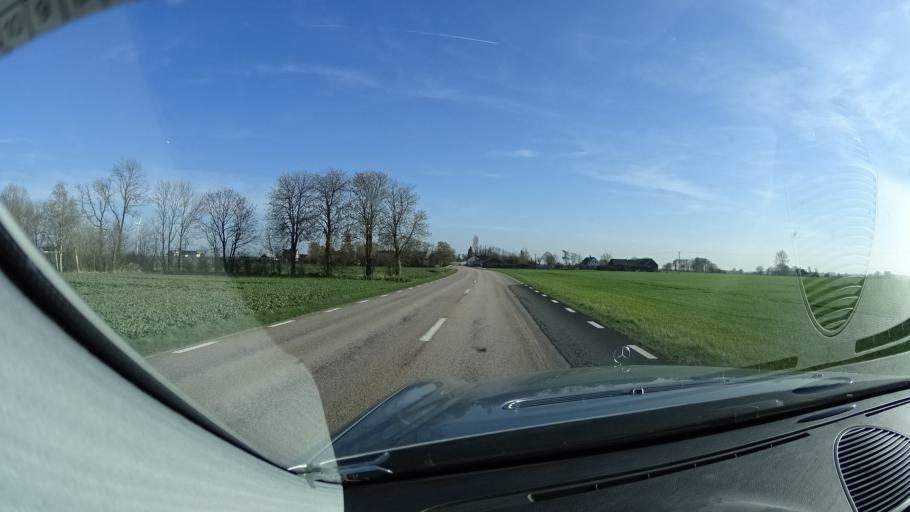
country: SE
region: Skane
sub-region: Landskrona
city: Asmundtorp
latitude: 55.9578
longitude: 12.9458
